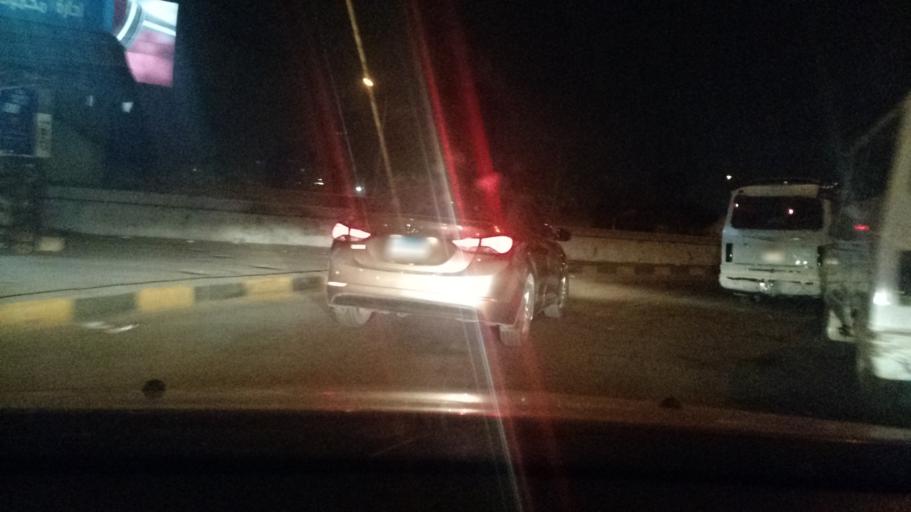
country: EG
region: Al Jizah
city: Al Jizah
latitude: 30.0157
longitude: 31.2168
